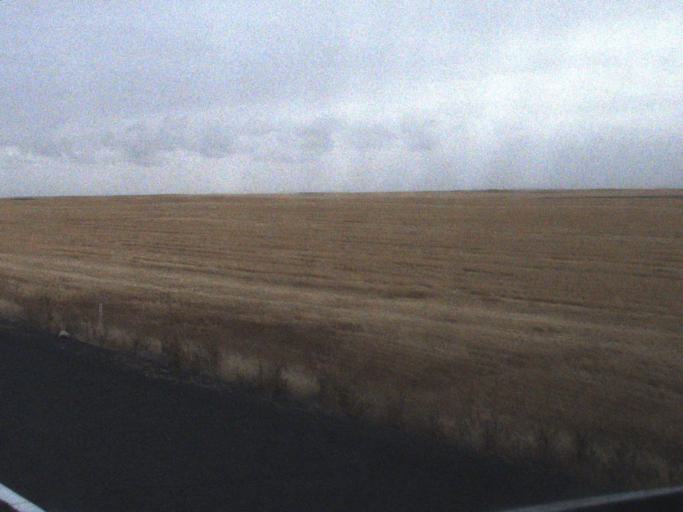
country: US
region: Washington
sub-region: Adams County
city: Ritzville
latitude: 46.7955
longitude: -118.4755
